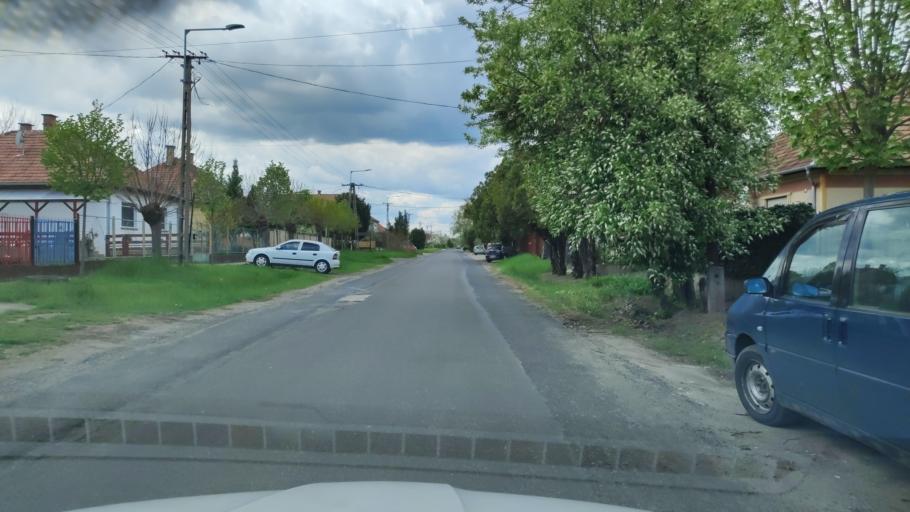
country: HU
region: Pest
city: Cegledbercel
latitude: 47.2112
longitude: 19.7265
